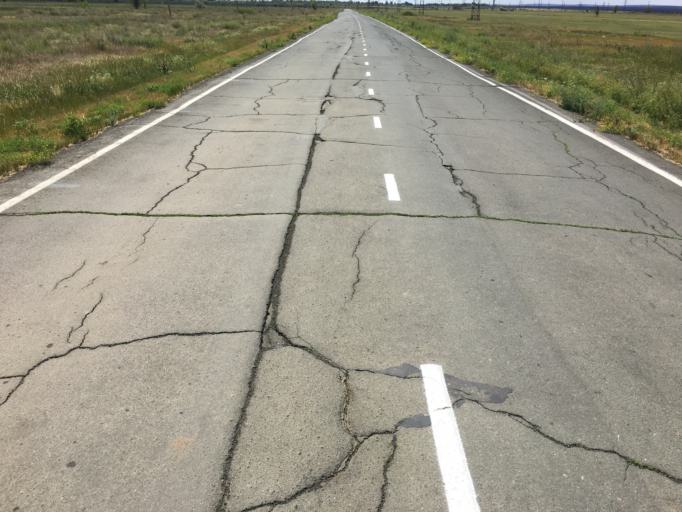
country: RU
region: Orenburg
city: Novotroitsk
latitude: 51.1555
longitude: 58.3408
